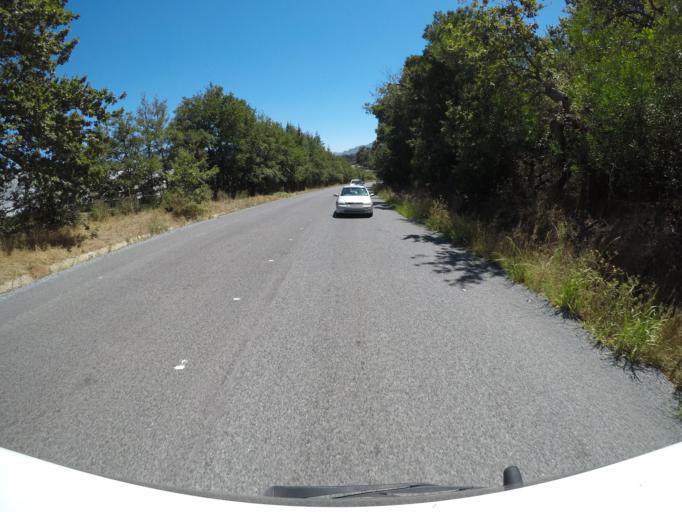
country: ZA
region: Western Cape
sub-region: Overberg District Municipality
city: Grabouw
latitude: -34.1718
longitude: 19.0346
